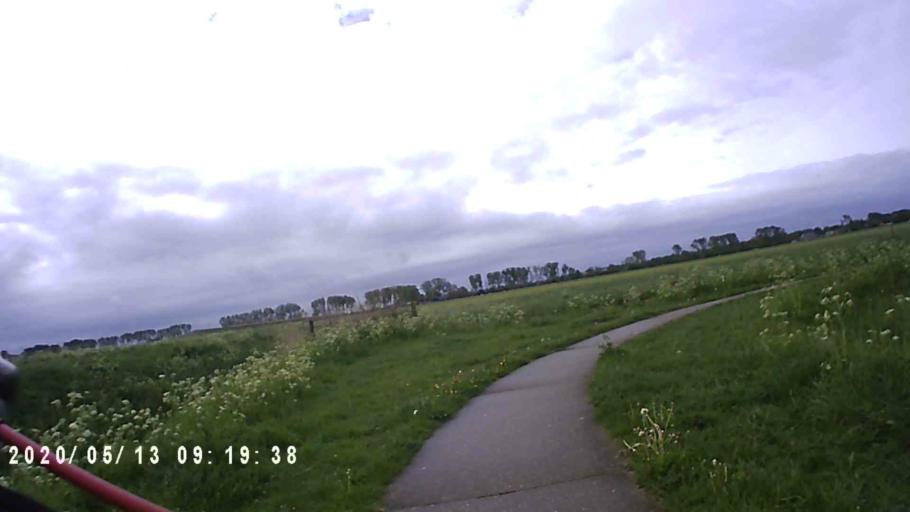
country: NL
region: Groningen
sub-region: Gemeente Zuidhorn
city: Noordhorn
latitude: 53.2640
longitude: 6.4072
